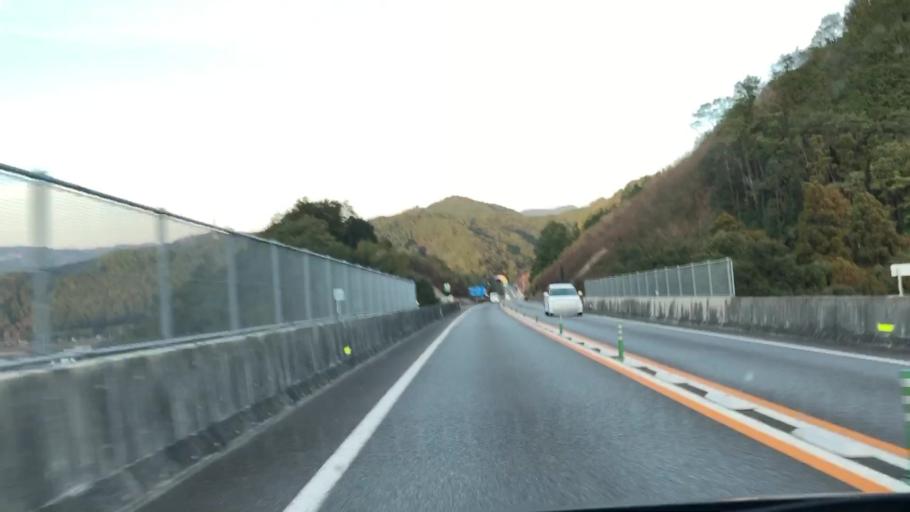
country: JP
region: Kumamoto
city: Minamata
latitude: 32.2765
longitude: 130.4957
